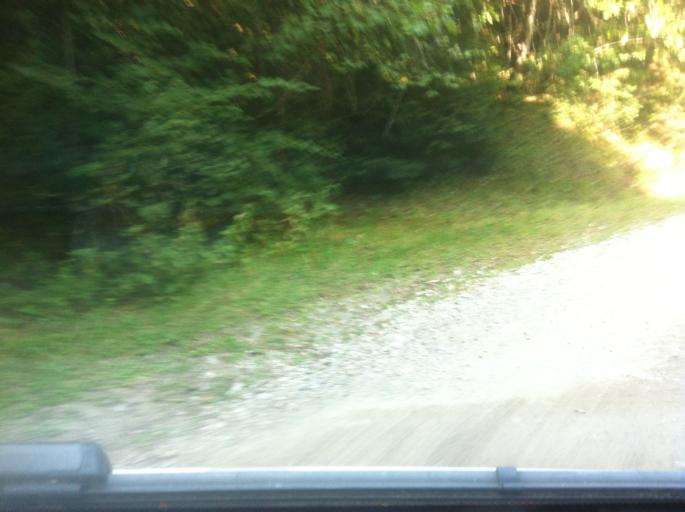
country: RO
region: Hunedoara
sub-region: Comuna Rau de Mori
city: Rau de Mori
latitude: 45.4407
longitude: 22.8917
